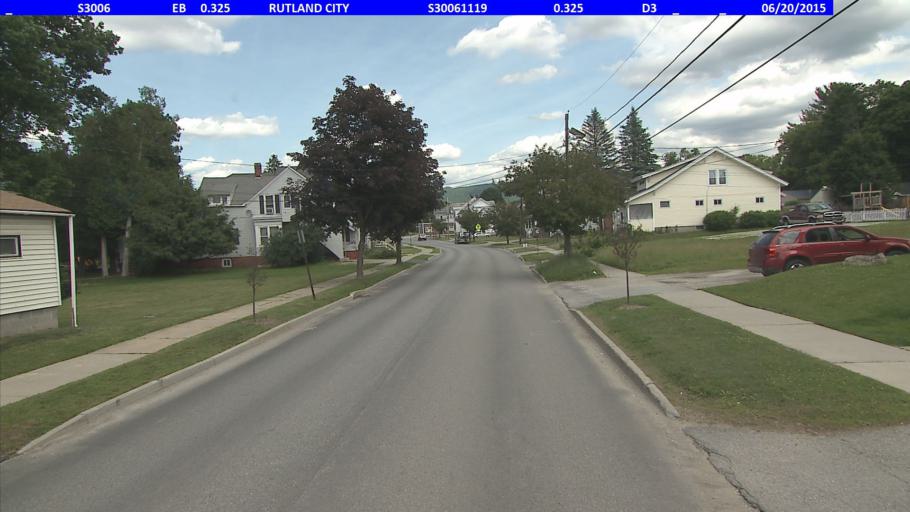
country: US
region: Vermont
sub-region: Rutland County
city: Rutland
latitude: 43.6149
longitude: -72.9854
